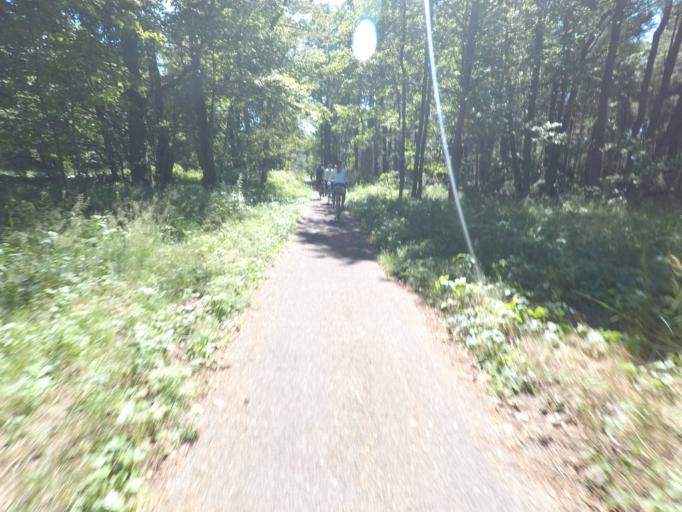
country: LT
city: Neringa
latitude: 55.4769
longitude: 21.0877
